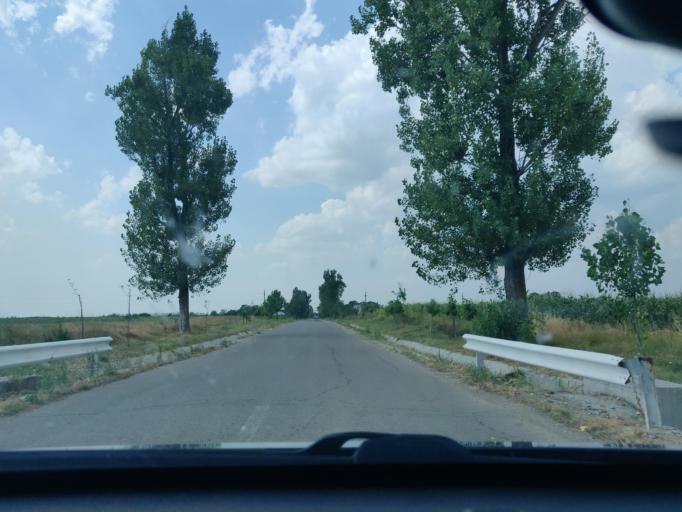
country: RO
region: Teleorman
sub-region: Comuna Sarbeni
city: Sarbeni
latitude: 44.4639
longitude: 25.3916
